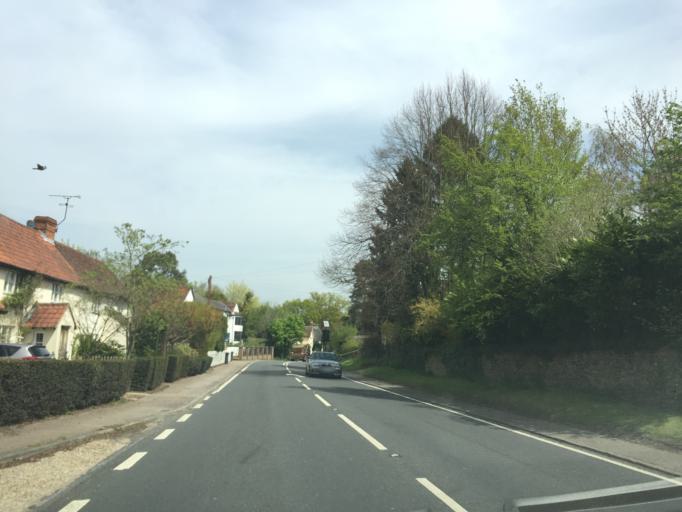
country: GB
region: England
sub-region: Essex
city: Elsenham
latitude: 51.9542
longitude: 0.2030
